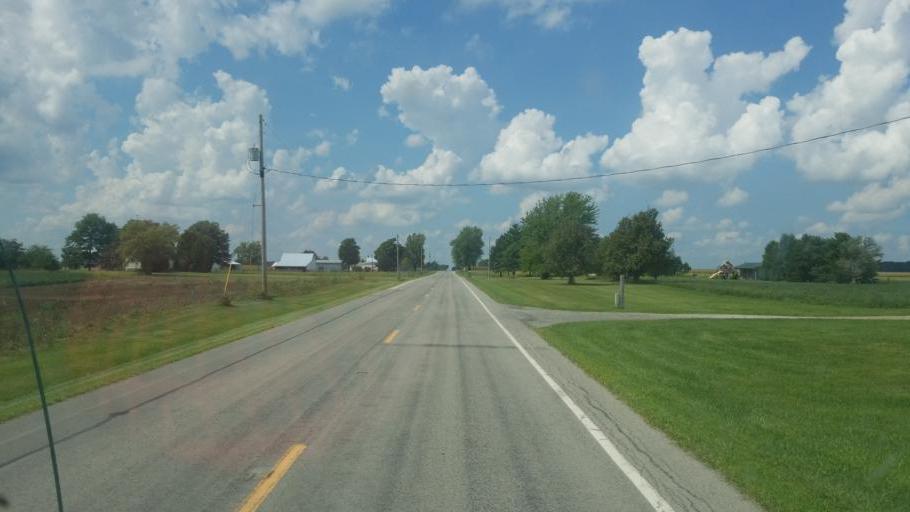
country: US
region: Ohio
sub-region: Hardin County
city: Kenton
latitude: 40.7321
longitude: -83.6604
